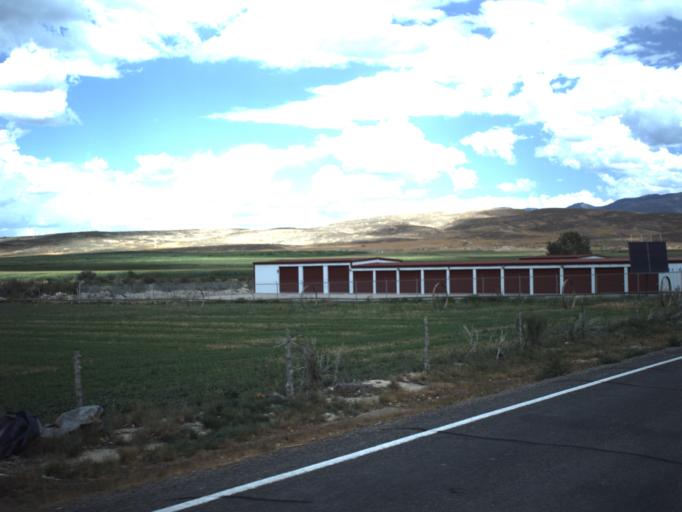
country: US
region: Utah
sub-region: Sanpete County
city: Gunnison
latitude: 39.1417
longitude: -111.7962
